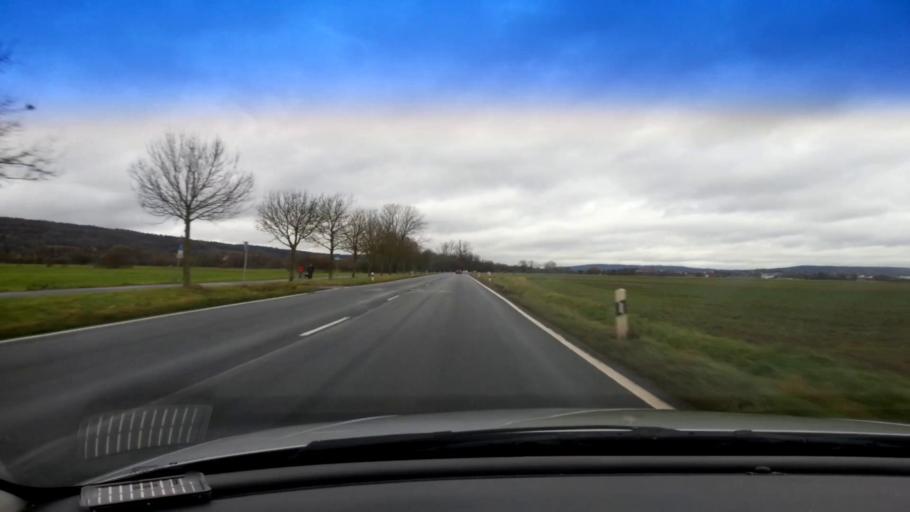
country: DE
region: Bavaria
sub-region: Upper Franconia
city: Breitengussbach
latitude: 49.9908
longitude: 10.8833
